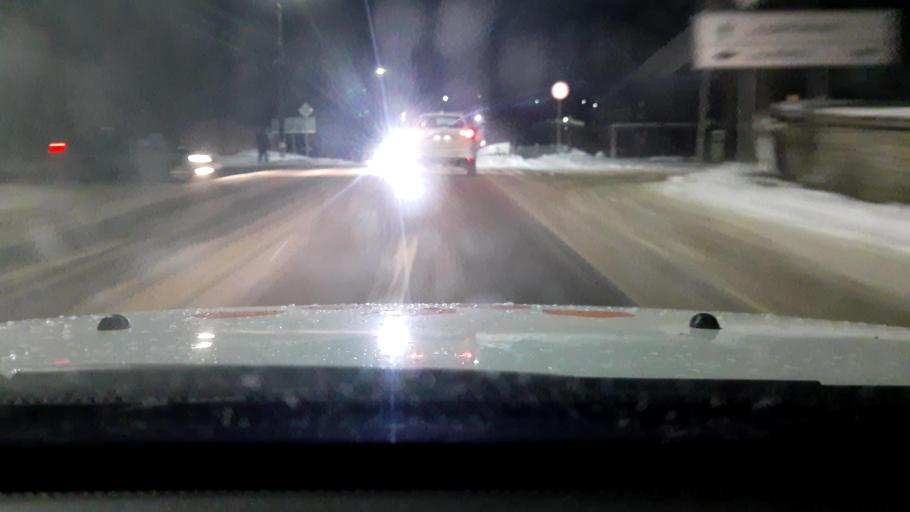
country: RU
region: Nizjnij Novgorod
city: Gorodets
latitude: 56.6576
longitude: 43.4799
